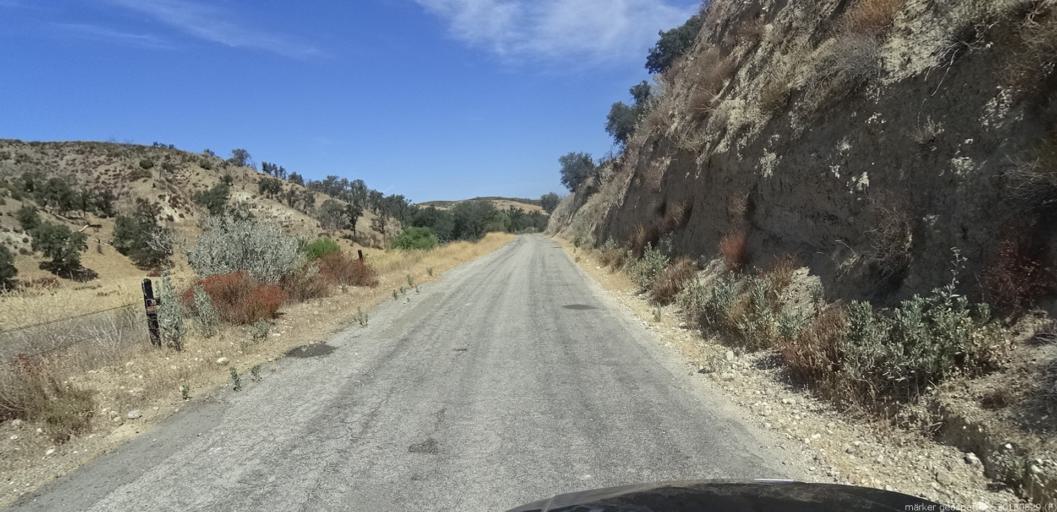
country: US
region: California
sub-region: San Luis Obispo County
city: Lake Nacimiento
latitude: 35.8542
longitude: -121.0358
